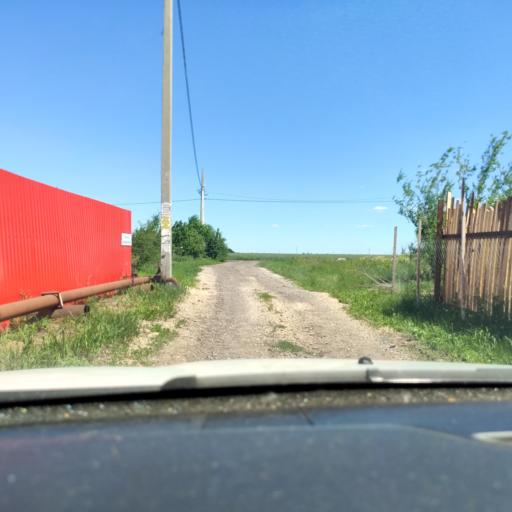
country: RU
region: Samara
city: Dubovyy Umet
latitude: 53.0270
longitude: 50.2517
